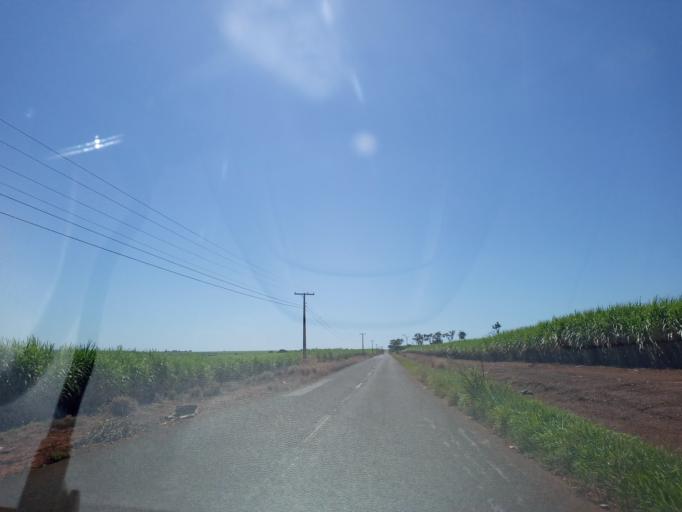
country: BR
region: Goias
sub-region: Itumbiara
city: Itumbiara
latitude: -18.4264
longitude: -49.1793
